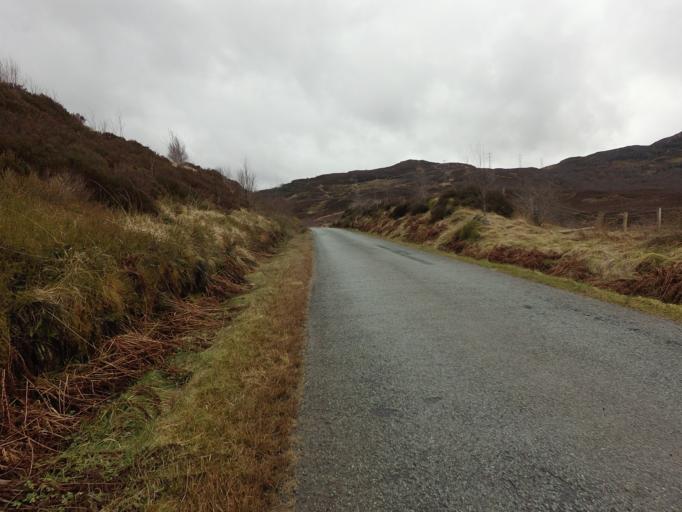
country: GB
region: Scotland
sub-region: West Dunbartonshire
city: Balloch
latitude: 56.2468
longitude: -4.5849
